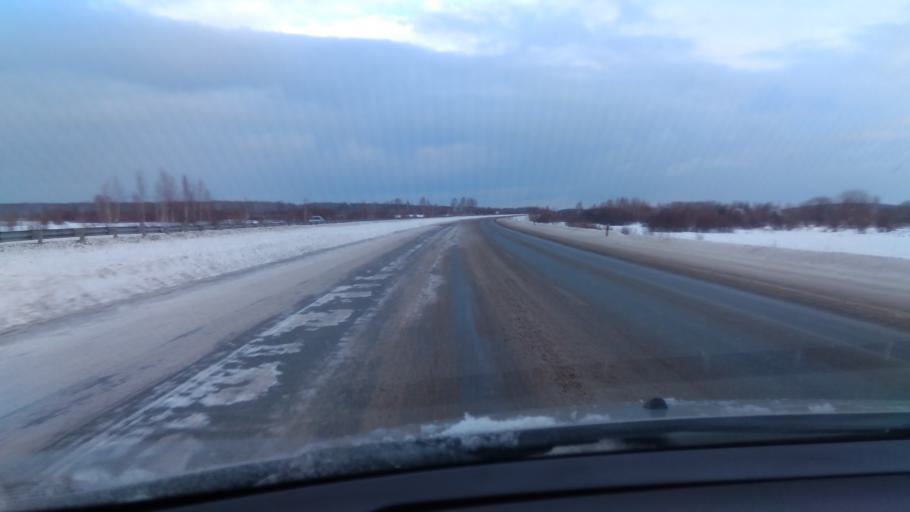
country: RU
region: Sverdlovsk
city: Nev'yansk
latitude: 57.5125
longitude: 60.1763
